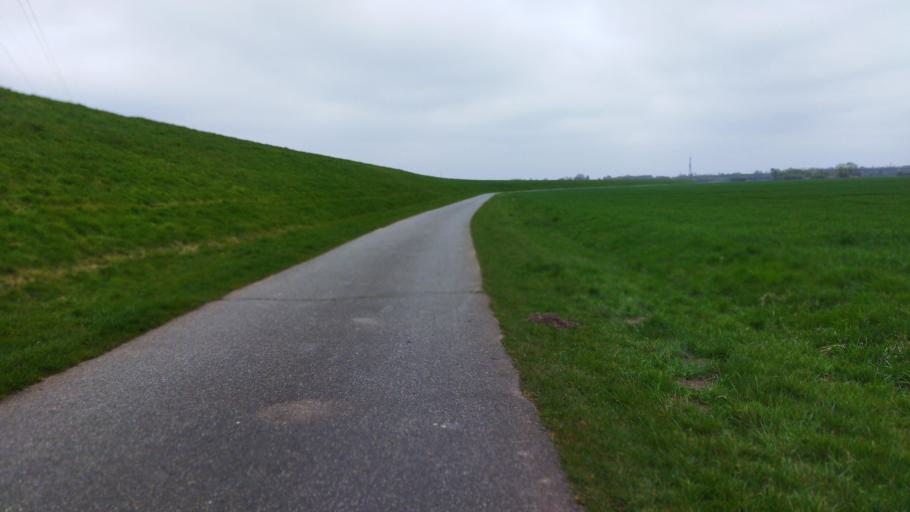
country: DE
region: Lower Saxony
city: Riede
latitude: 53.0196
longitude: 8.9001
